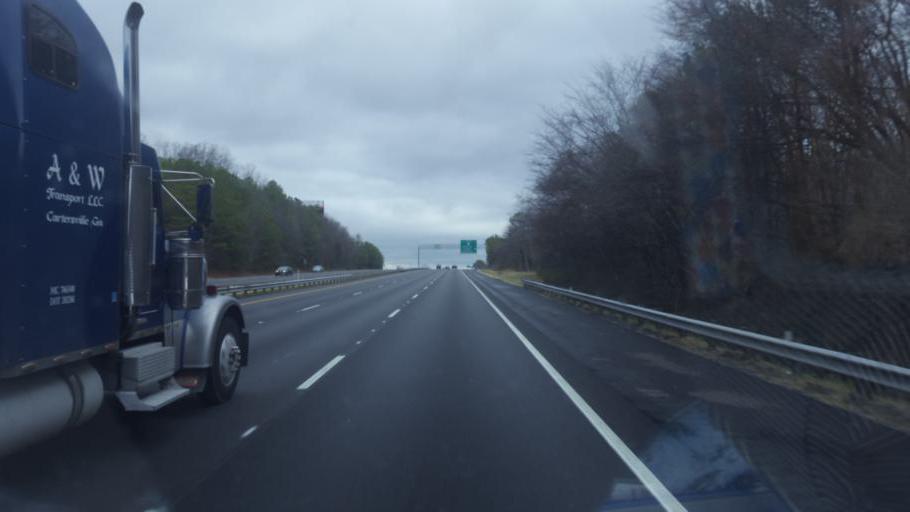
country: US
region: Georgia
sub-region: Catoosa County
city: Indian Springs
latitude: 34.9222
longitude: -85.1490
